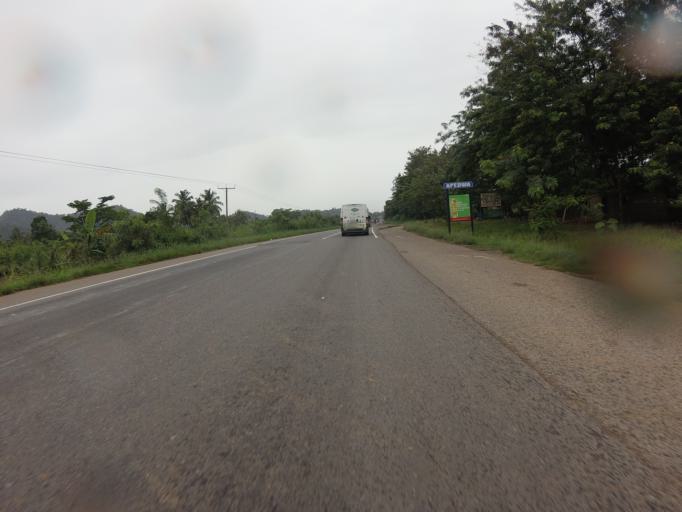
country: GH
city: Kibi
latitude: 6.1272
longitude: -0.4953
